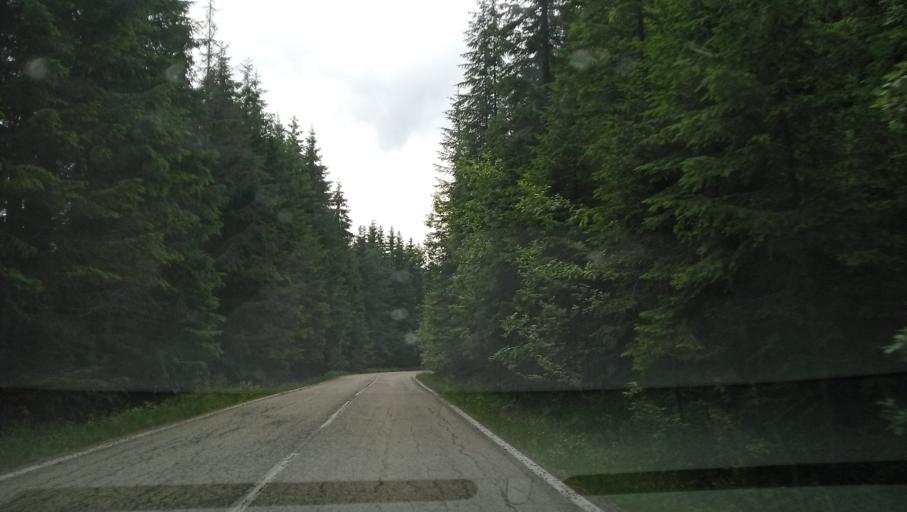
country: RO
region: Valcea
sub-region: Comuna Voineasa
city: Voineasa
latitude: 45.4205
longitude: 23.7547
